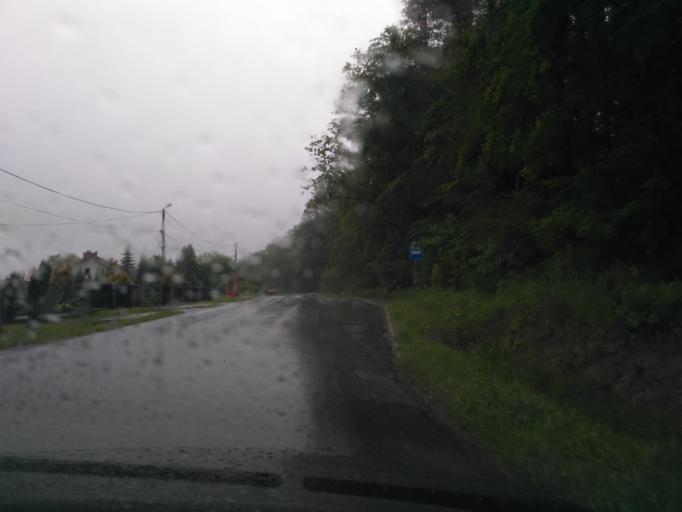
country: PL
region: Subcarpathian Voivodeship
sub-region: Powiat jasielski
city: Debowiec
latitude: 49.6583
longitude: 21.4228
